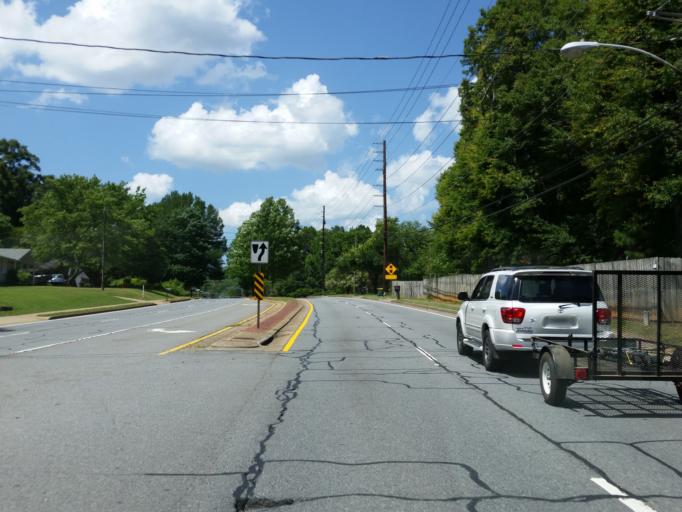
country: US
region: Georgia
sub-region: Cherokee County
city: Woodstock
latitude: 34.0444
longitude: -84.4568
